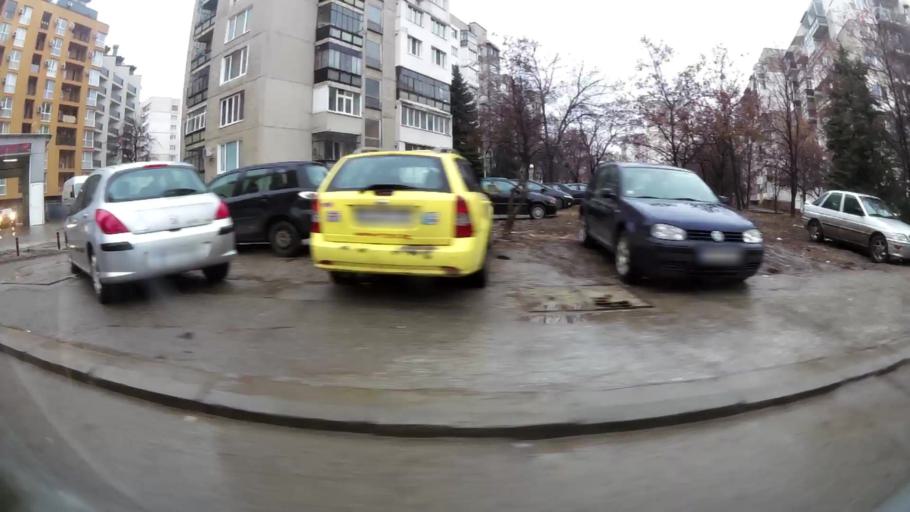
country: BG
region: Sofia-Capital
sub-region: Stolichna Obshtina
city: Sofia
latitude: 42.6269
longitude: 23.3840
